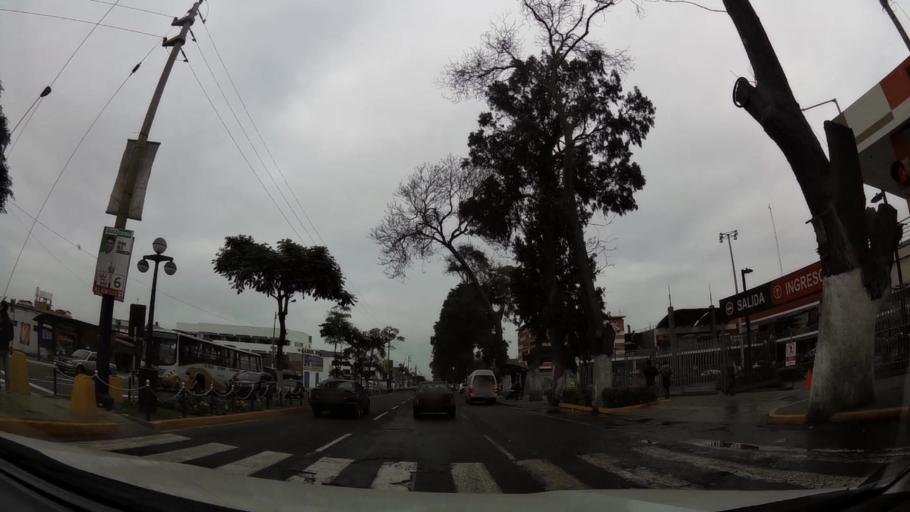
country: PE
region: Lima
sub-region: Lima
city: Surco
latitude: -12.1968
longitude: -77.0111
